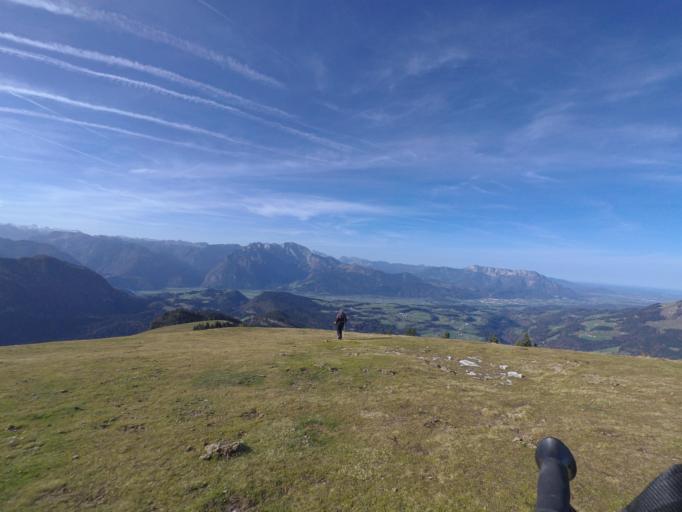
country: AT
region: Salzburg
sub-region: Politischer Bezirk Salzburg-Umgebung
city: Hintersee
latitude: 47.6405
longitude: 13.2718
